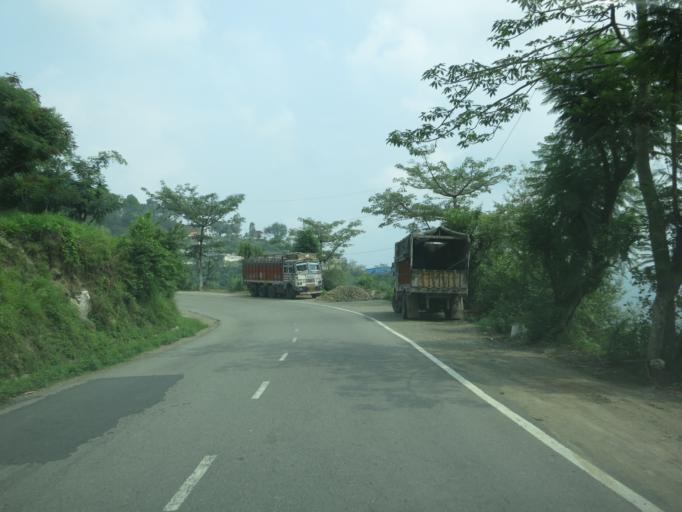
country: IN
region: Himachal Pradesh
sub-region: Bilaspur
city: Bilaspur
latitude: 31.2568
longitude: 76.8727
